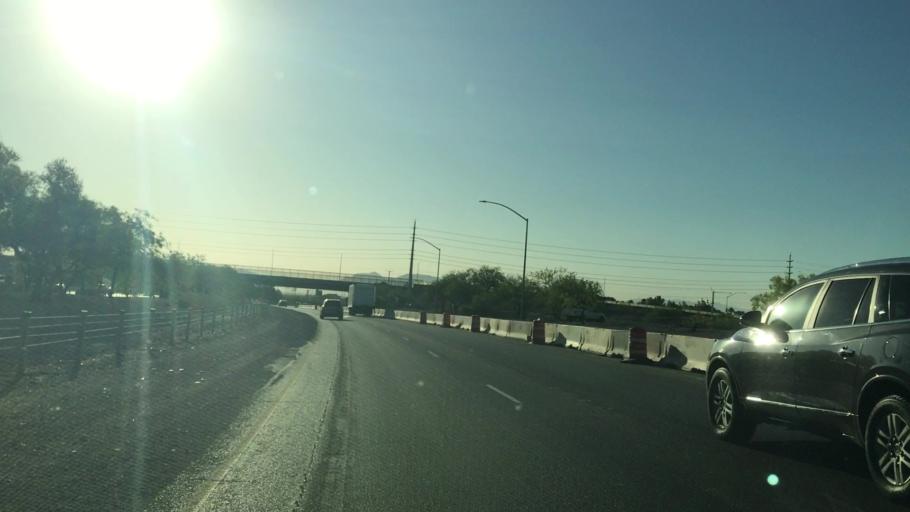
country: US
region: Nevada
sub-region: Clark County
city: Summerlin South
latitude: 36.1773
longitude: -115.2814
